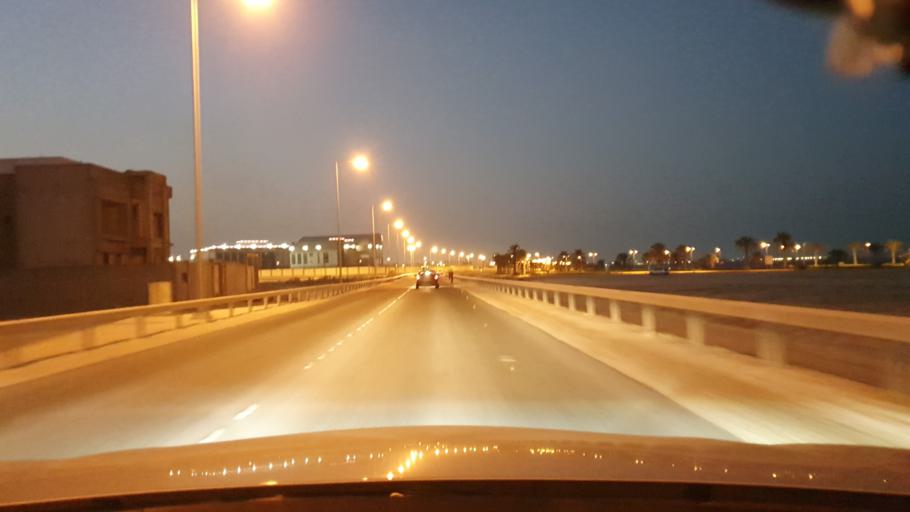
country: BH
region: Northern
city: Ar Rifa'
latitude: 26.0428
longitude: 50.6210
